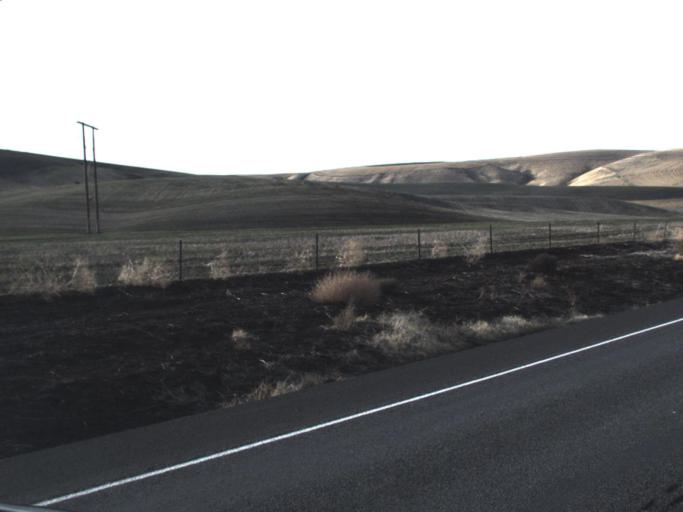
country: US
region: Washington
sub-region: Columbia County
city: Dayton
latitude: 46.5342
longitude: -117.8500
